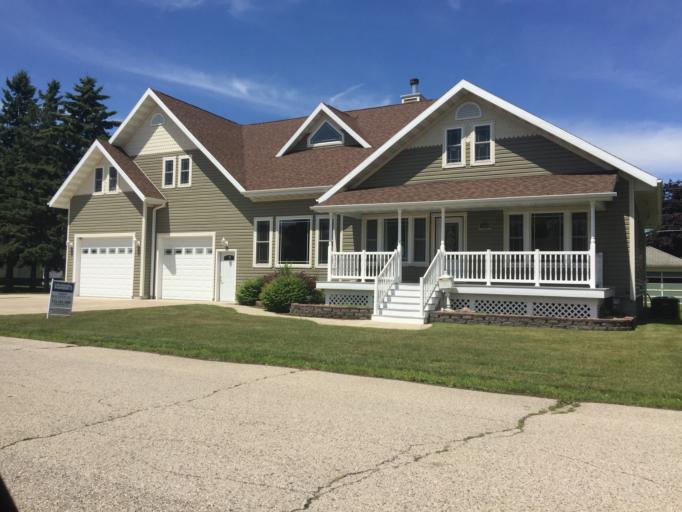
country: US
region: Wisconsin
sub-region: Marinette County
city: Marinette
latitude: 45.1135
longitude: -87.6331
